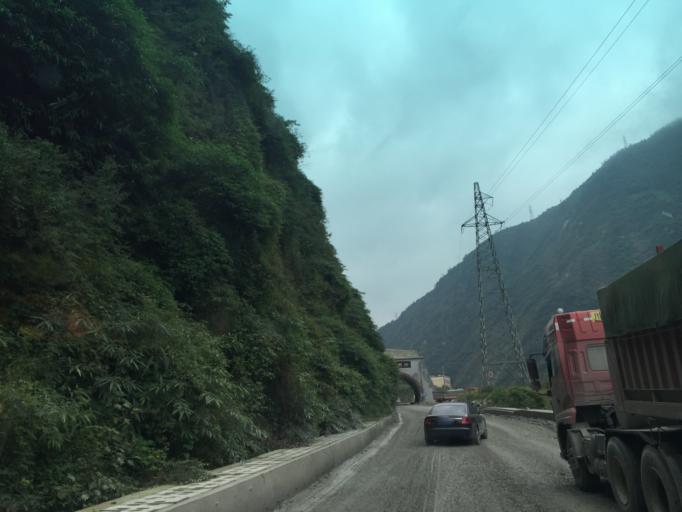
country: CN
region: Sichuan
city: Guangsheng
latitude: 31.0834
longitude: 103.4853
